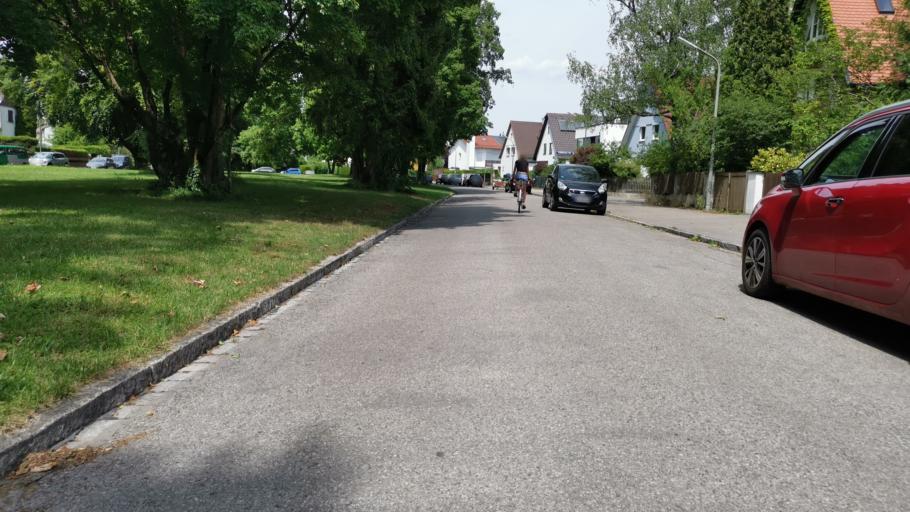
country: DE
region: Bavaria
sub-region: Upper Bavaria
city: Pullach im Isartal
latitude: 48.0908
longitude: 11.5141
